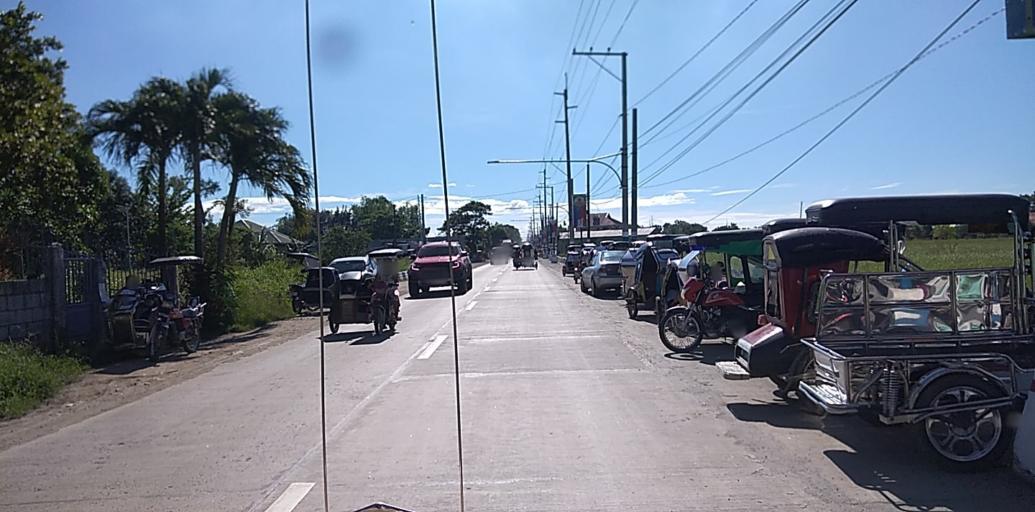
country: PH
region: Central Luzon
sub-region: Province of Pampanga
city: San Luis
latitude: 15.0526
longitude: 120.7803
